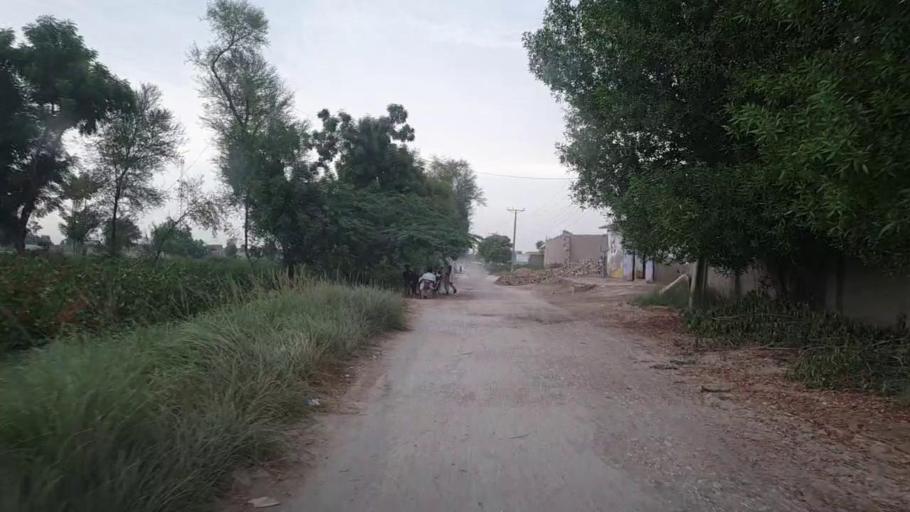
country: PK
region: Sindh
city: Karaundi
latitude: 26.9841
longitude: 68.3437
